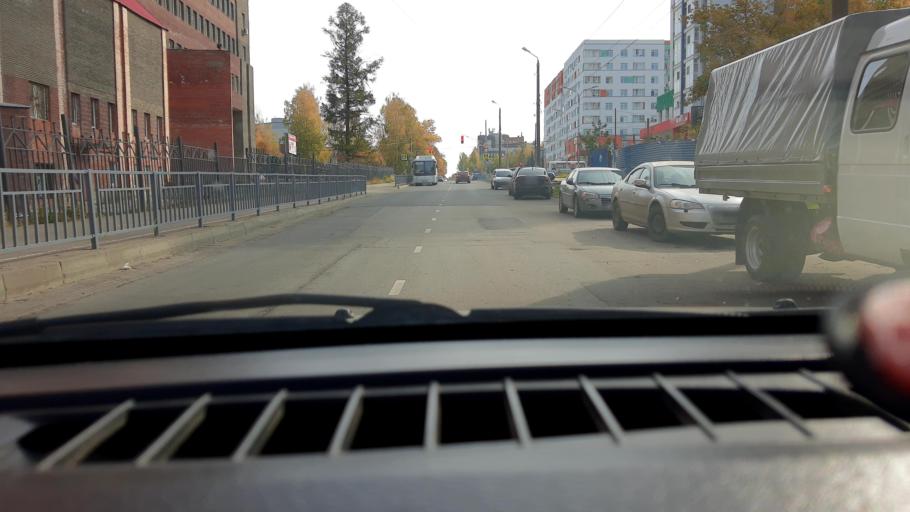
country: RU
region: Nizjnij Novgorod
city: Kstovo
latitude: 56.1525
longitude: 44.1860
